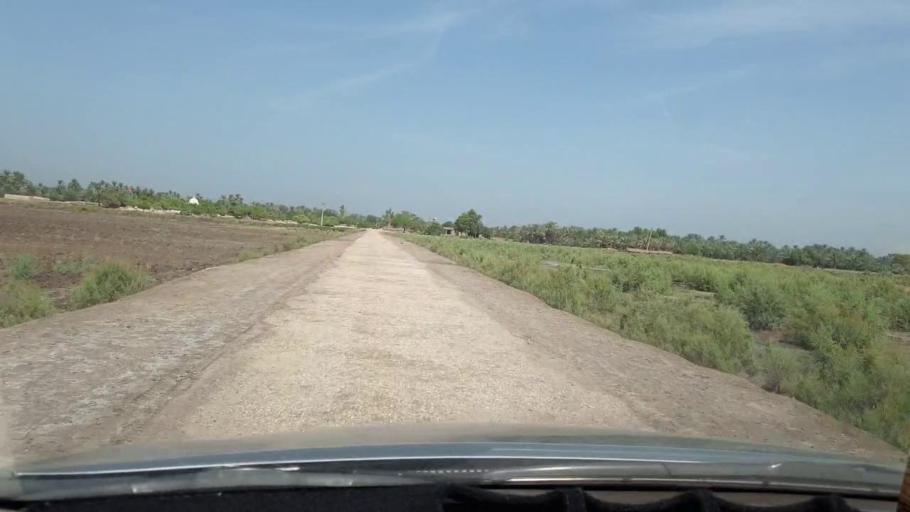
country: PK
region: Sindh
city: Khairpur
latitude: 27.4718
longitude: 68.7439
